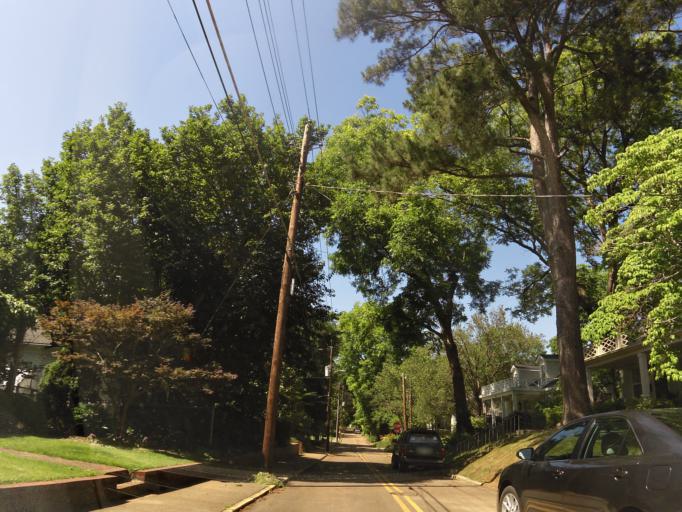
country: US
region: Mississippi
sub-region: Lafayette County
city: Oxford
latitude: 34.3604
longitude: -89.5209
